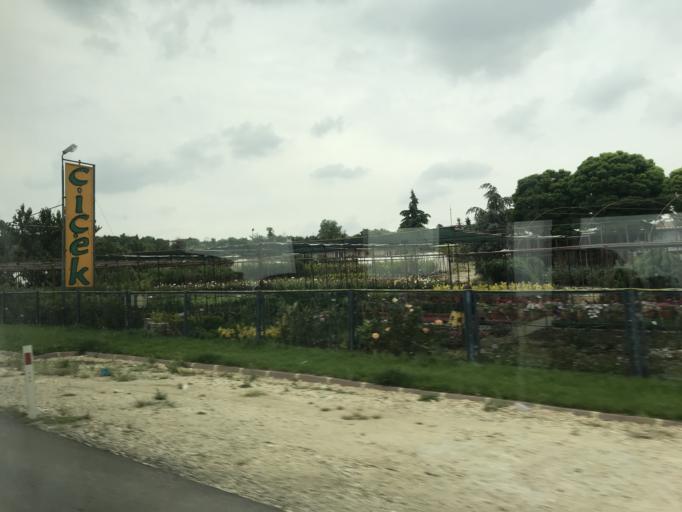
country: TR
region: Tekirdag
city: Malkara
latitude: 40.8654
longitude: 26.8002
